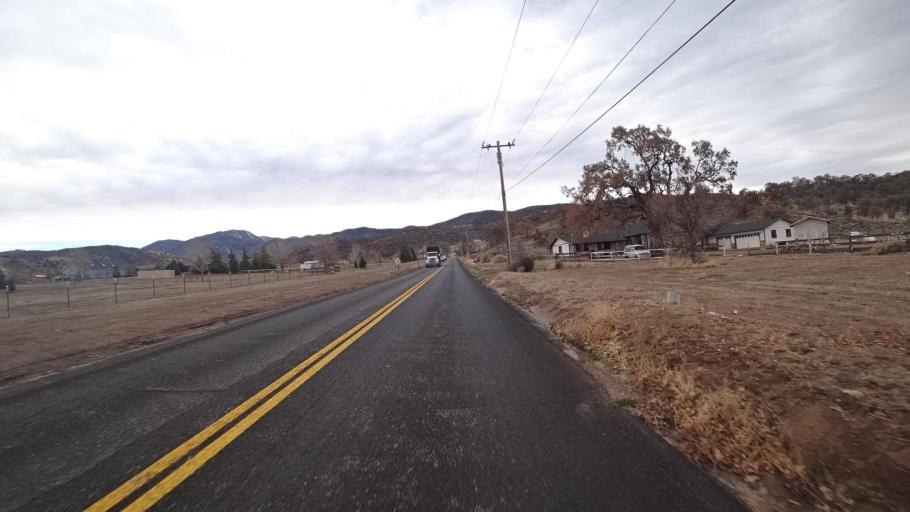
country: US
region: California
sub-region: Kern County
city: Golden Hills
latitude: 35.1012
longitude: -118.5373
